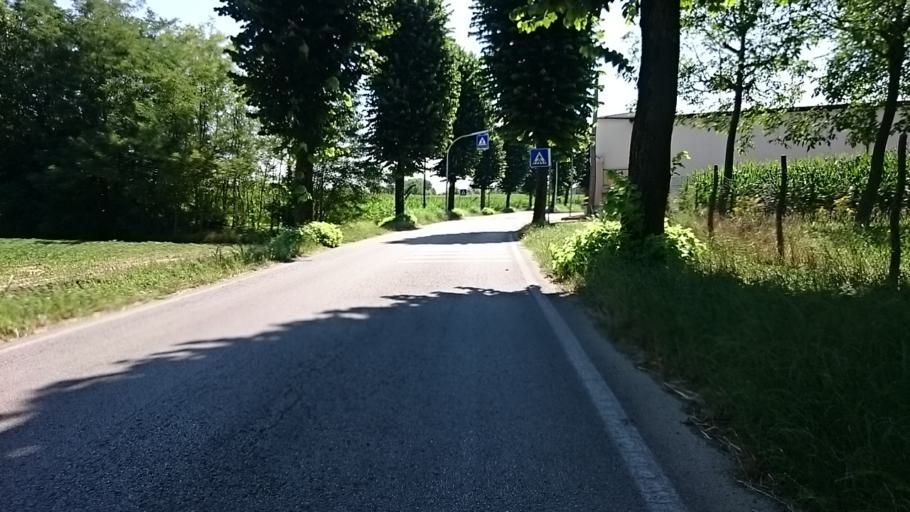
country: IT
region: Veneto
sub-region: Provincia di Padova
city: Saccolongo
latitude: 45.4162
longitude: 11.7356
